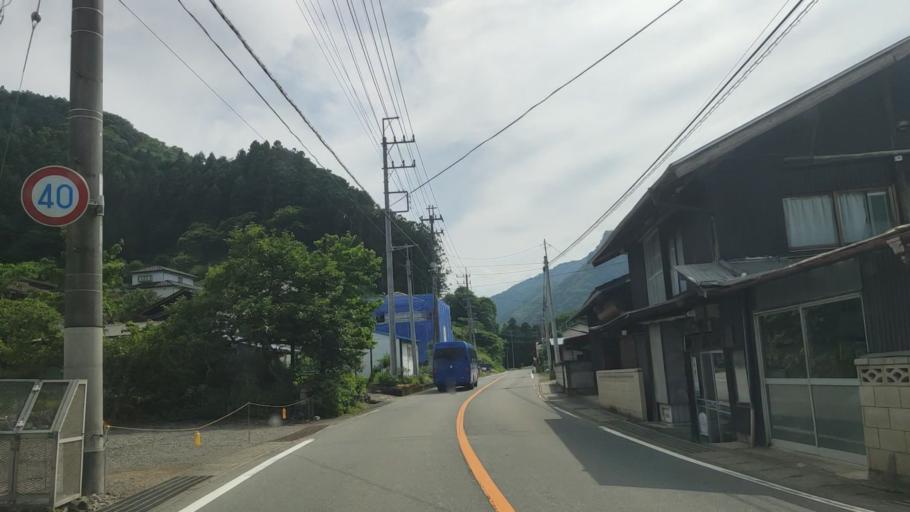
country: JP
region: Gunma
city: Tomioka
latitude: 36.2018
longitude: 138.7658
